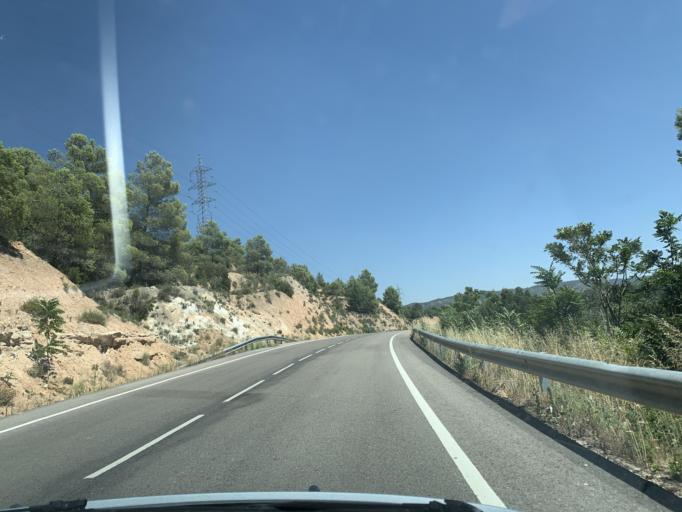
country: ES
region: Castille-La Mancha
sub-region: Provincia de Guadalajara
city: Zorita de los Canes
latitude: 40.3587
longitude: -2.9080
